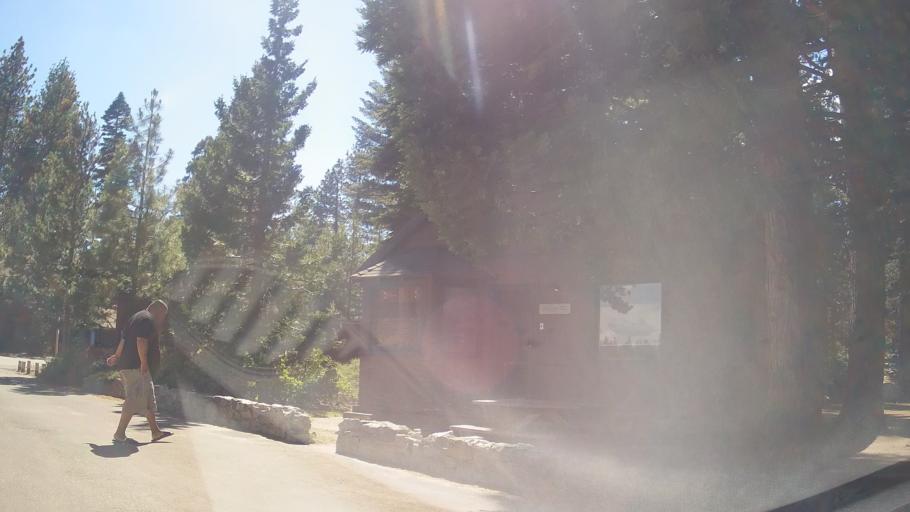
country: US
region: California
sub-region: Placer County
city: Tahoma
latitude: 39.0391
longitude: -120.1227
